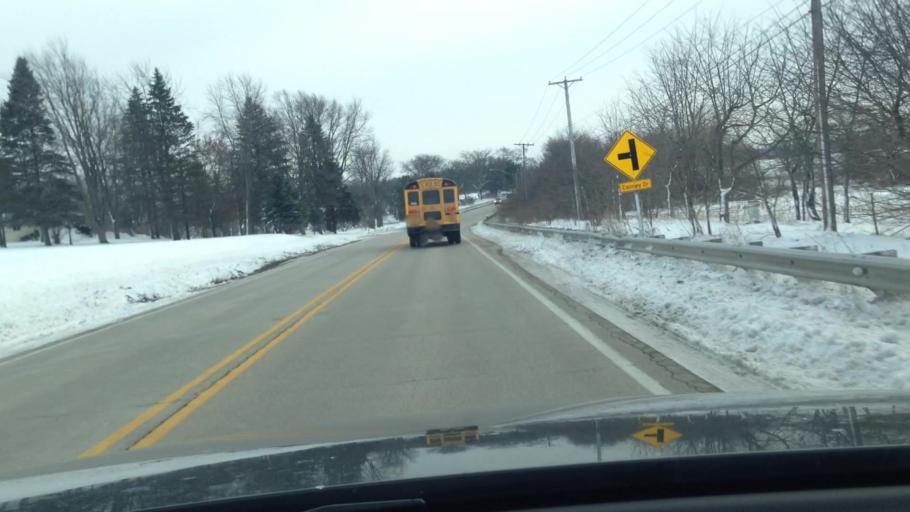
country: US
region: Illinois
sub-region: McHenry County
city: Woodstock
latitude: 42.3557
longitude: -88.4431
